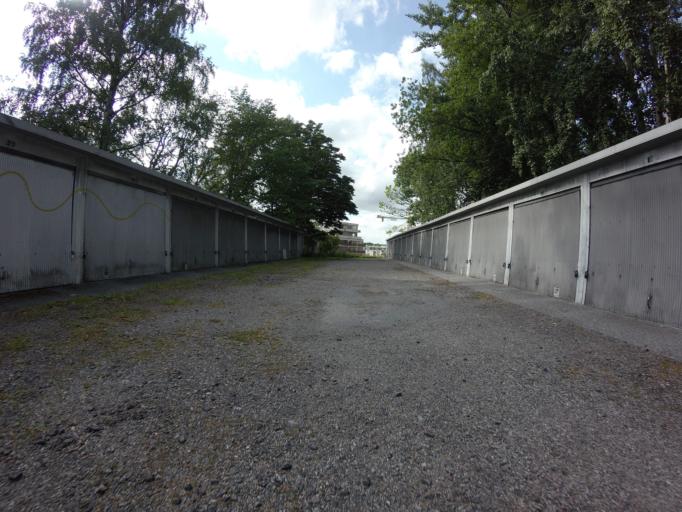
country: SE
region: Stockholm
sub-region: Stockholms Kommun
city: OEstermalm
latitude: 59.3544
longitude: 18.0916
